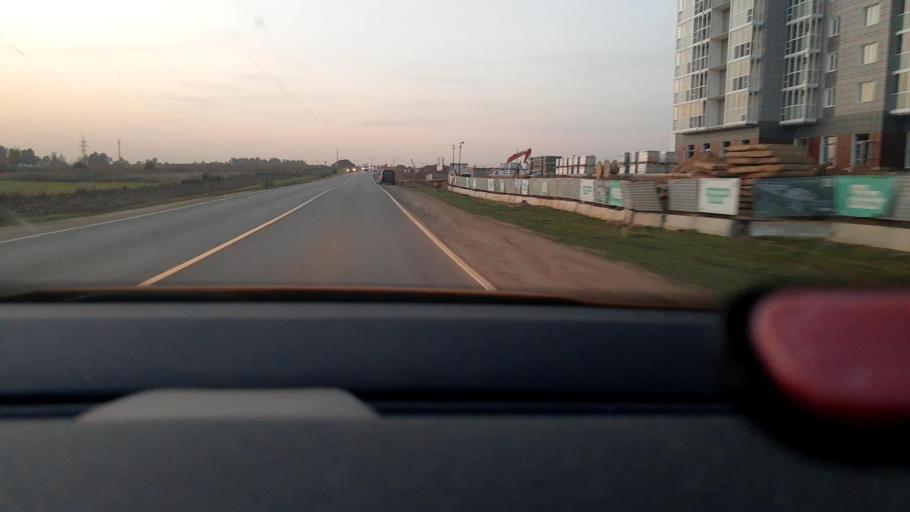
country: RU
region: Moskovskaya
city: Filimonki
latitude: 55.5324
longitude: 37.3760
